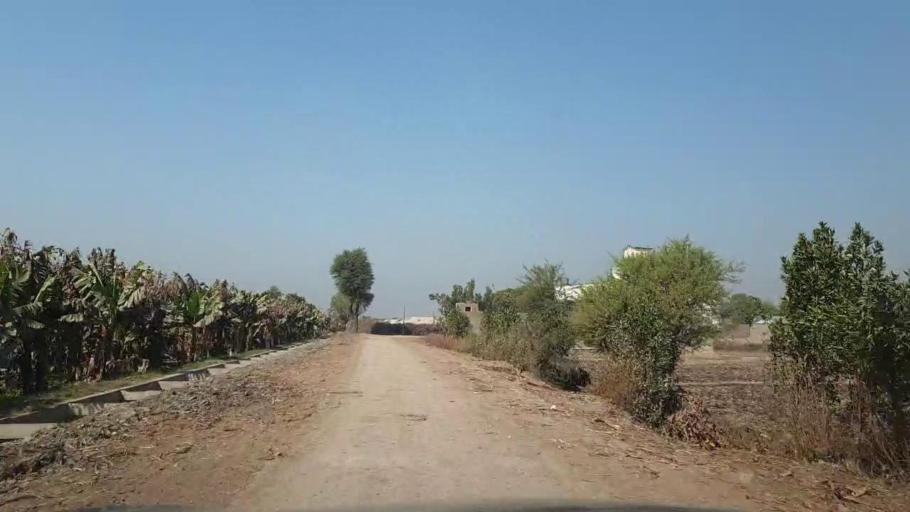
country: PK
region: Sindh
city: Tando Allahyar
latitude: 25.5282
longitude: 68.6641
